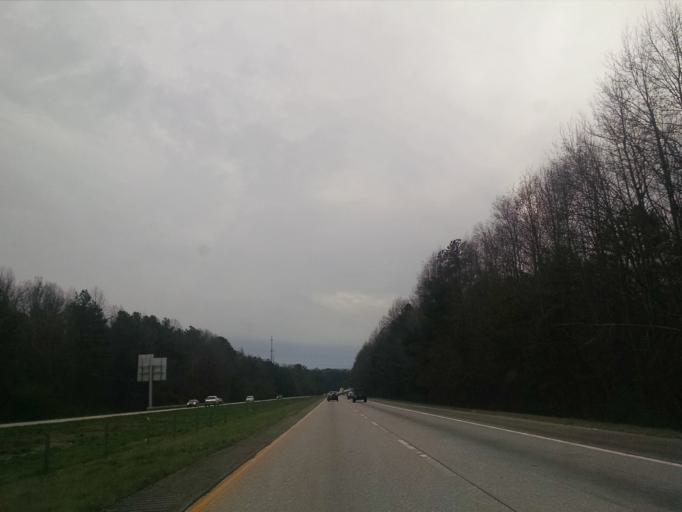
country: US
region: Georgia
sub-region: Hall County
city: Oakwood
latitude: 34.2043
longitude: -83.8909
